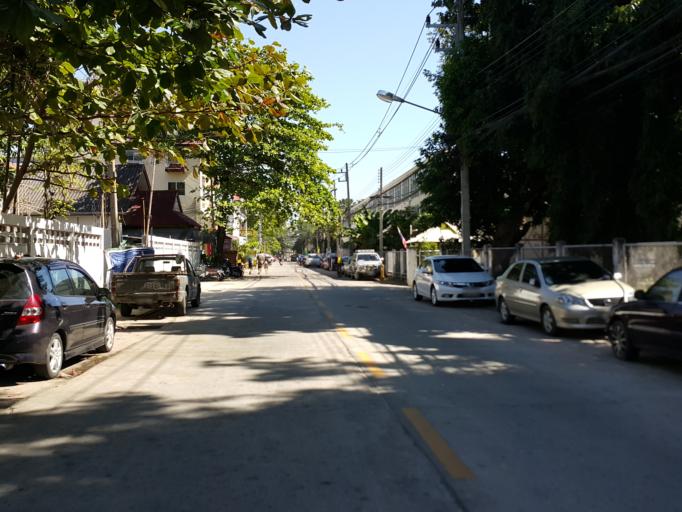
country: TH
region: Chiang Mai
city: Chiang Mai
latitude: 18.7931
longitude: 98.9846
